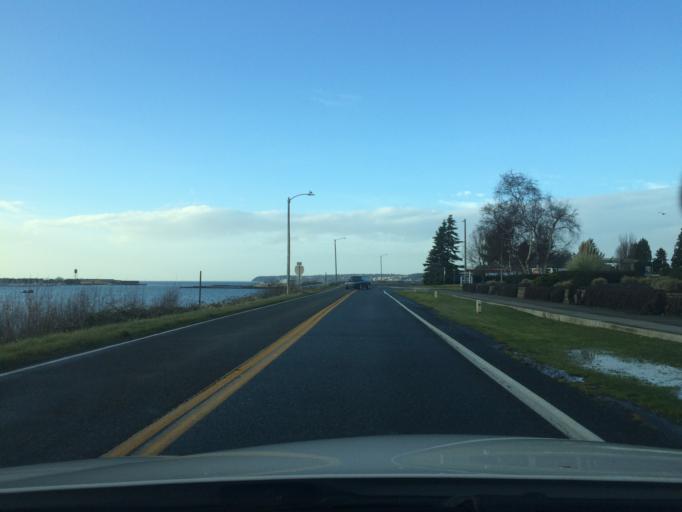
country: US
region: Washington
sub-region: Whatcom County
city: Blaine
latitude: 48.9869
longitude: -122.7489
